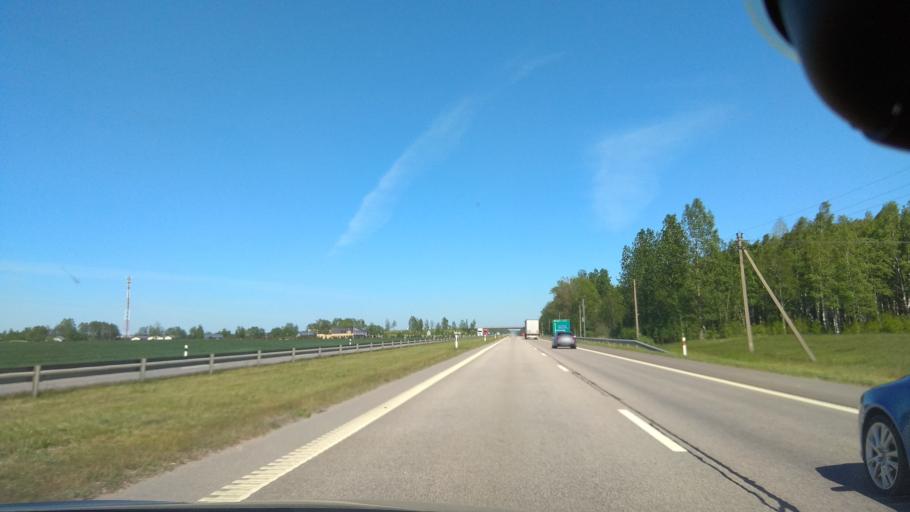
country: LT
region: Klaipedos apskritis
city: Gargzdai
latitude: 55.7201
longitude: 21.3035
